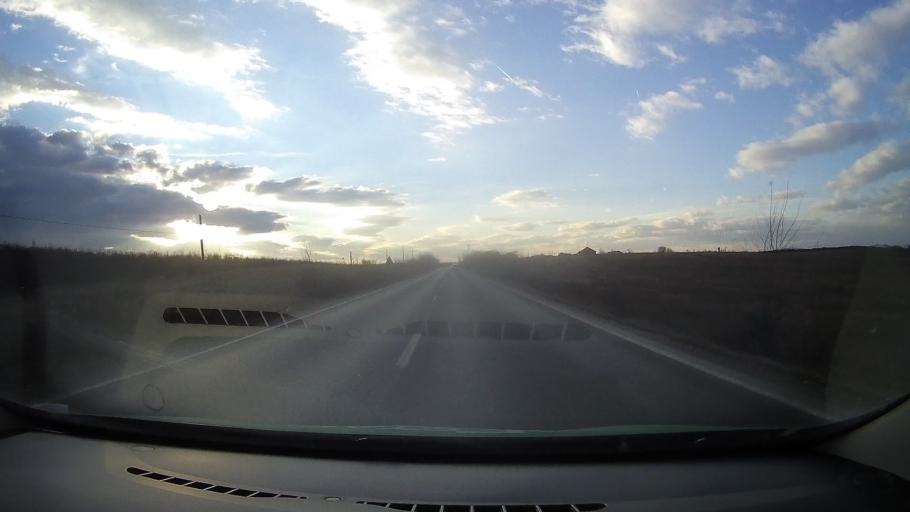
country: RO
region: Dambovita
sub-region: Comuna I. L. Caragiale
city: Mija
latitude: 44.9114
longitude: 25.6836
